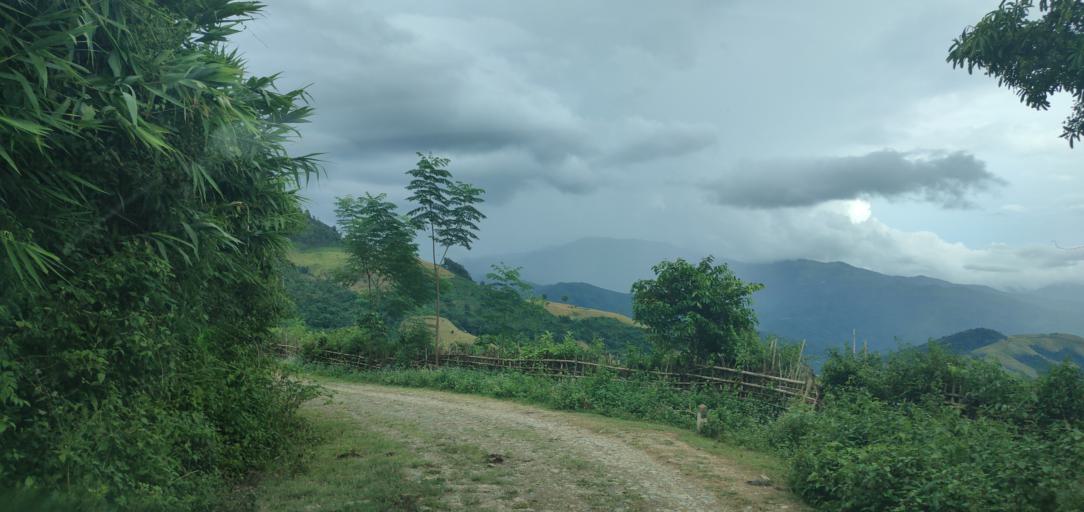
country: LA
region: Phongsali
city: Phongsali
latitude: 21.4461
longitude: 102.3042
